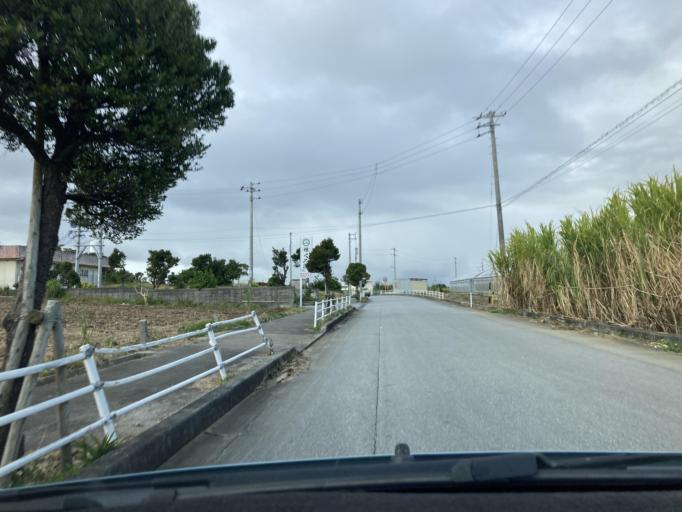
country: JP
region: Okinawa
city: Itoman
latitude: 26.1259
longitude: 127.6866
